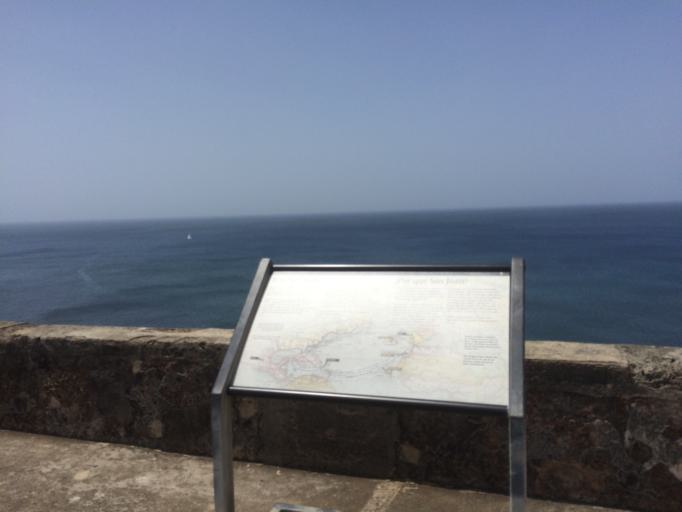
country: PR
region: San Juan
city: San Juan
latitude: 18.4678
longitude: -66.1110
